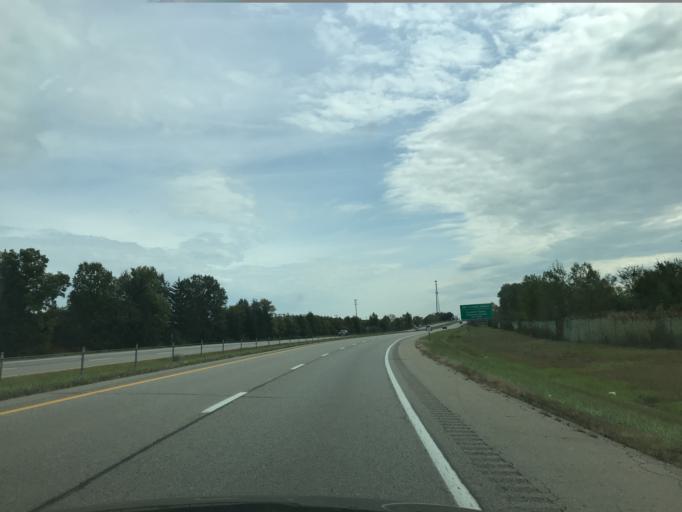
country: US
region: Ohio
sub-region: Trumbull County
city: Champion Heights
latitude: 41.2758
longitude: -80.8580
